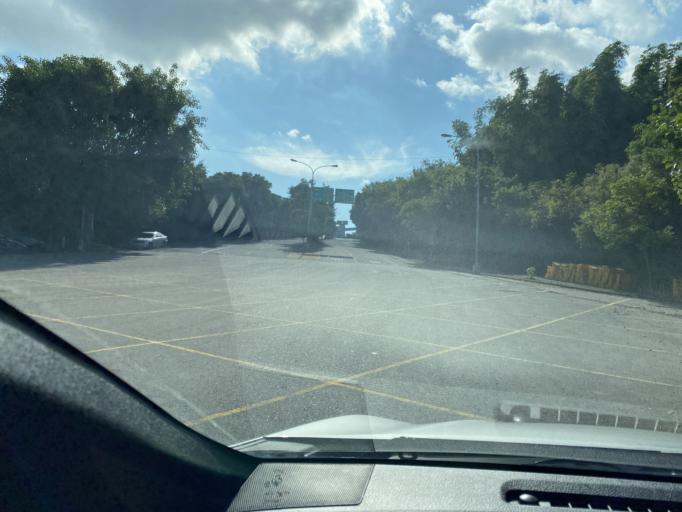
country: TW
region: Taiwan
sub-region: Changhua
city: Chang-hua
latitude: 24.0652
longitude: 120.5552
